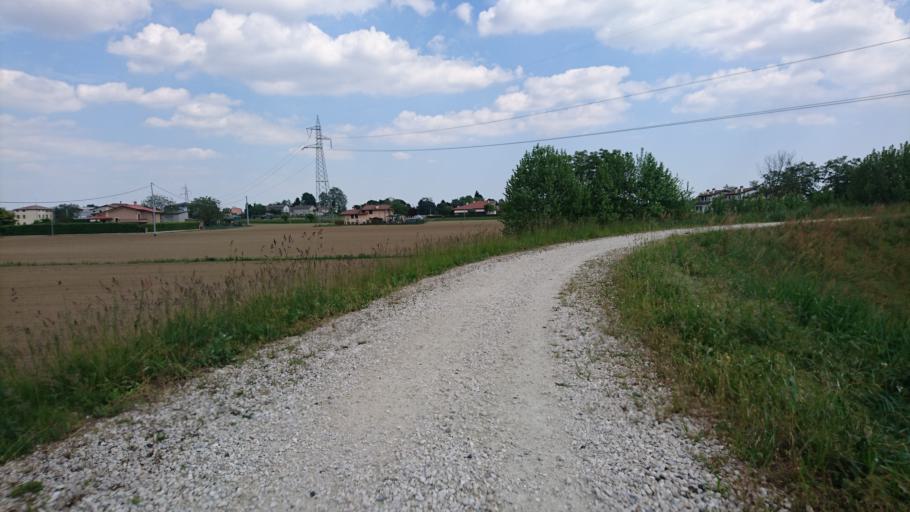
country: IT
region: Veneto
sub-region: Provincia di Padova
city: Veggiano
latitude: 45.4448
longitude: 11.7257
